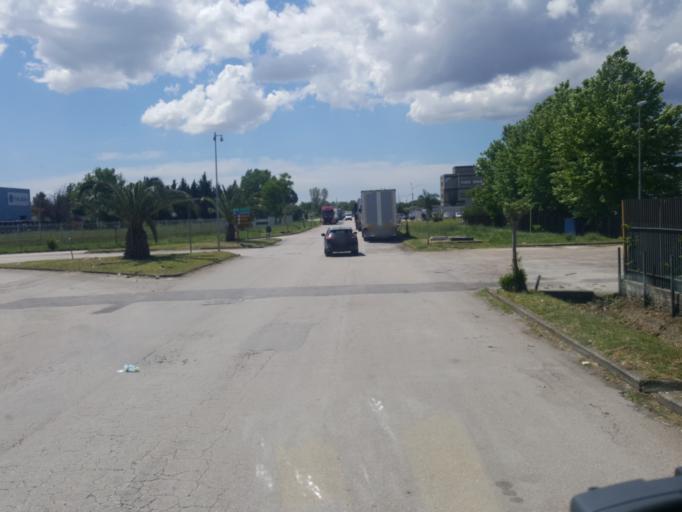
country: IT
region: Campania
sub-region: Provincia di Napoli
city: Pascarola
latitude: 40.9846
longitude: 14.3014
